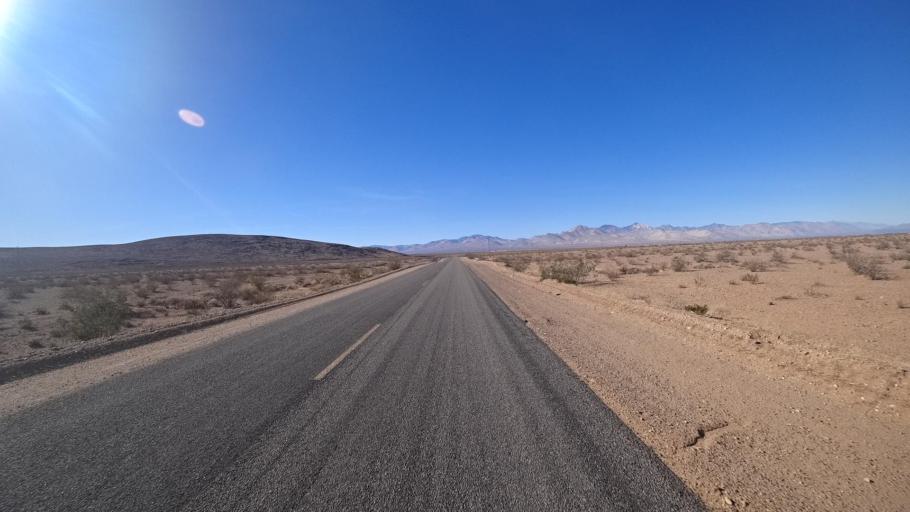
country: US
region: California
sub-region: Kern County
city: China Lake Acres
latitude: 35.5577
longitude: -117.7531
